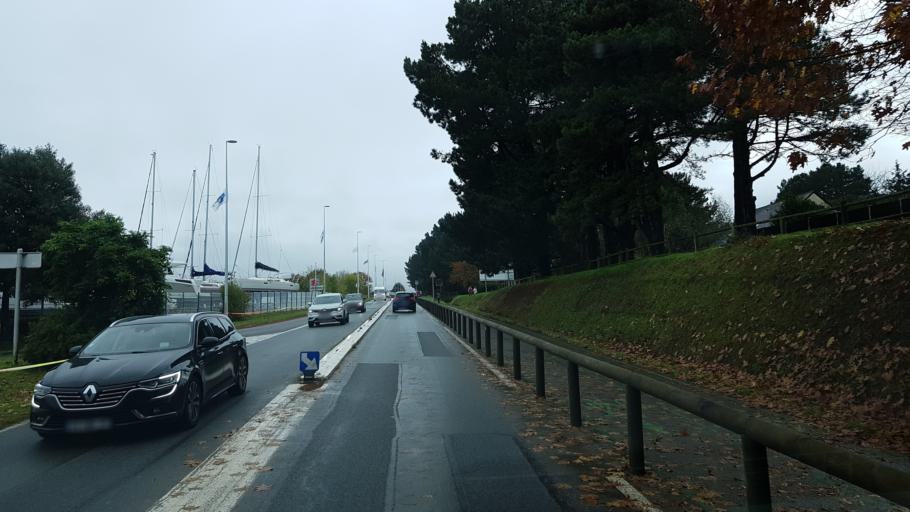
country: FR
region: Brittany
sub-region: Departement du Morbihan
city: Arzon
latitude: 47.5448
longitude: -2.8864
